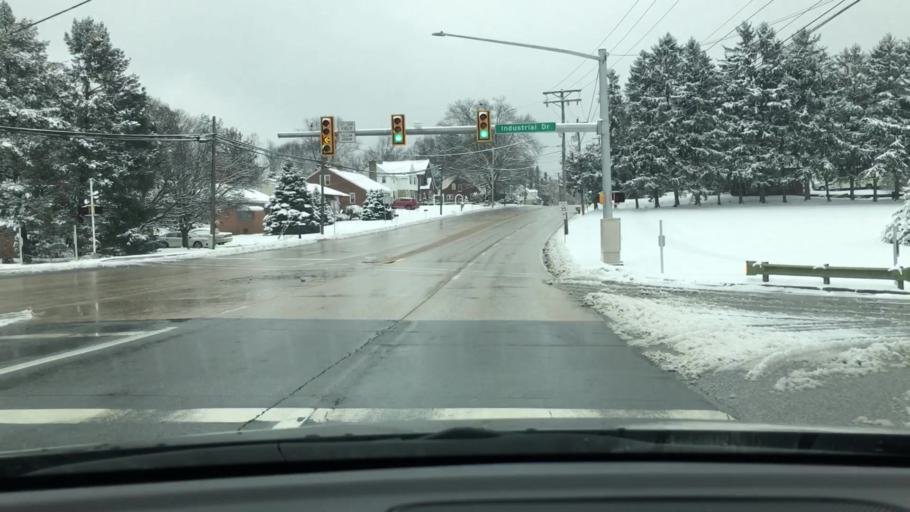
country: US
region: Pennsylvania
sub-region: York County
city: Yorklyn
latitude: 39.9825
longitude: -76.6642
